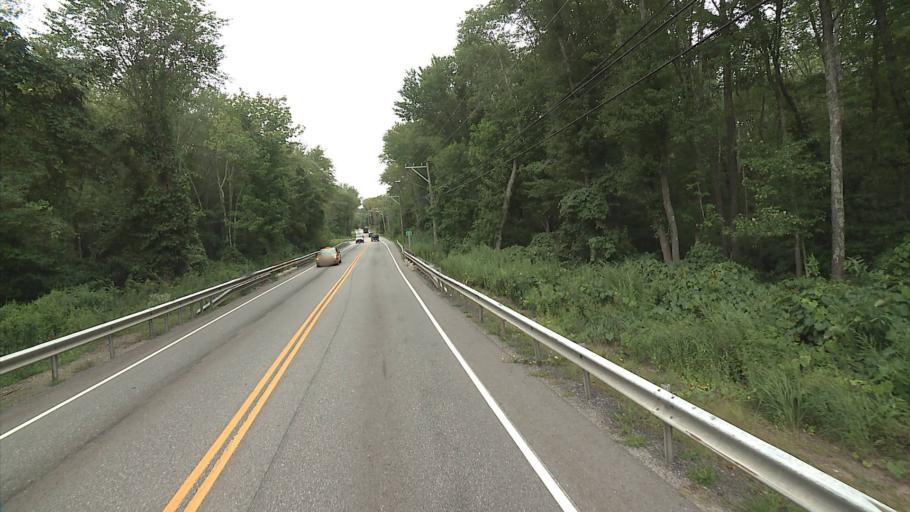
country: US
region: Connecticut
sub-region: New London County
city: Montville Center
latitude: 41.4371
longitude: -72.2256
